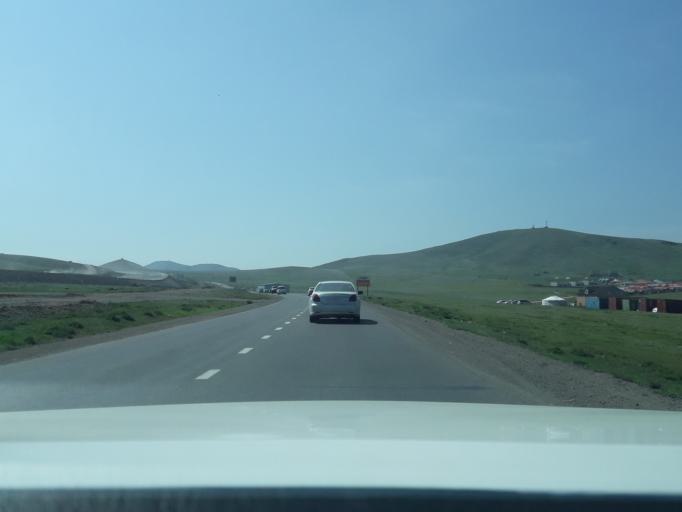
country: MN
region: Ulaanbaatar
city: Ulaanbaatar
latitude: 47.8012
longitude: 106.7469
